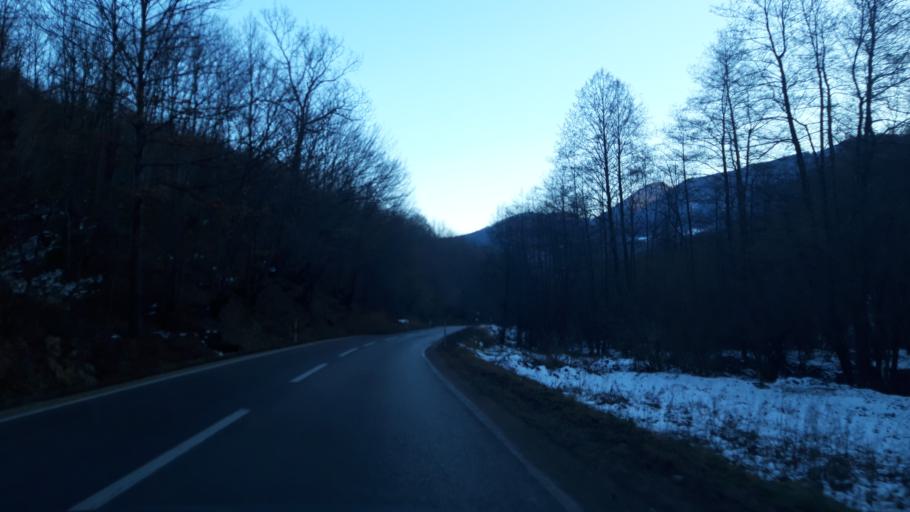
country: BA
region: Republika Srpska
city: Vlasenica
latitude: 44.1764
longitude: 19.0115
